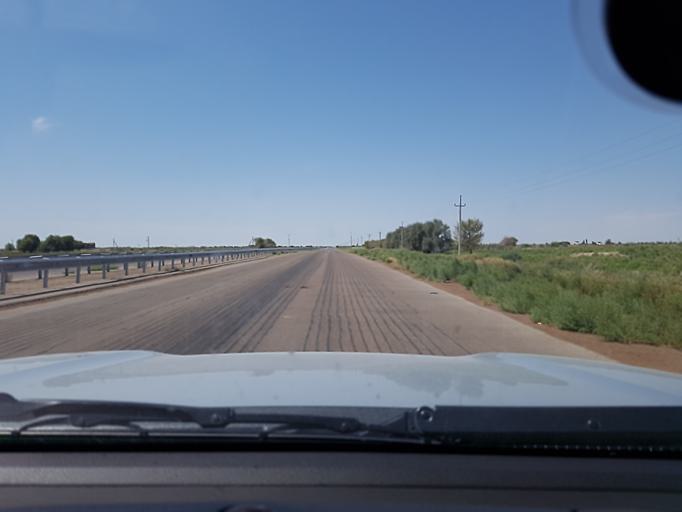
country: TM
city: Akdepe
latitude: 41.7362
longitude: 59.0714
